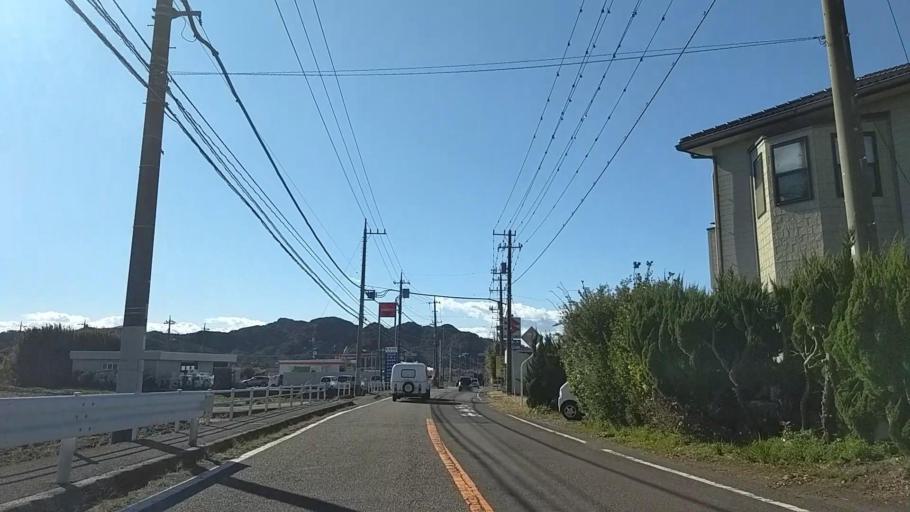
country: JP
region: Chiba
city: Tateyama
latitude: 34.9328
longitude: 139.8392
